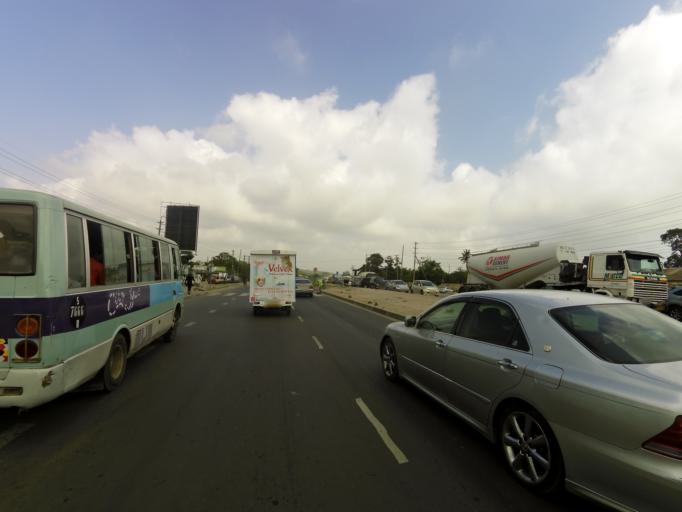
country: TZ
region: Dar es Salaam
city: Magomeni
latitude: -6.7630
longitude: 39.2278
